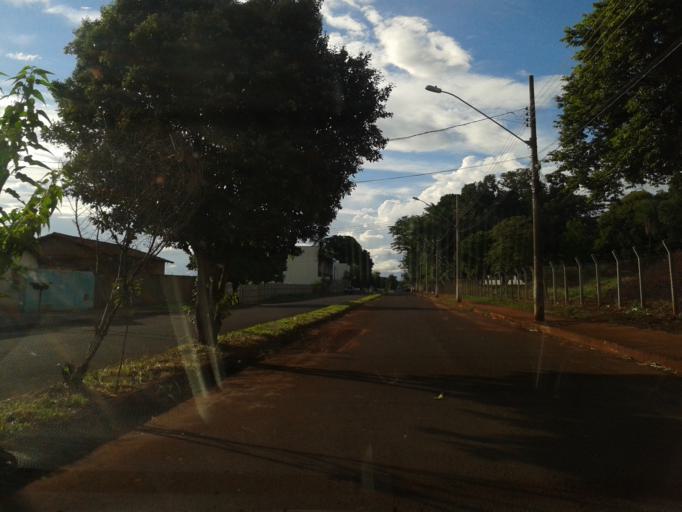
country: BR
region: Minas Gerais
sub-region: Ituiutaba
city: Ituiutaba
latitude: -18.9740
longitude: -49.4473
